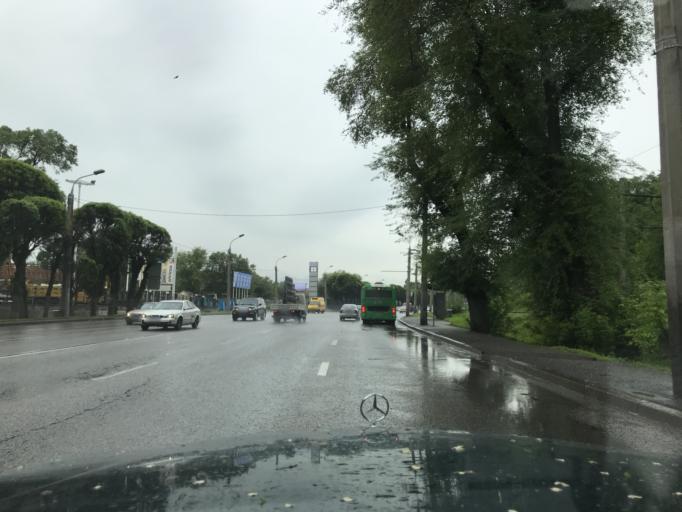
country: KZ
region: Almaty Qalasy
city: Almaty
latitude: 43.3000
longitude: 76.9512
